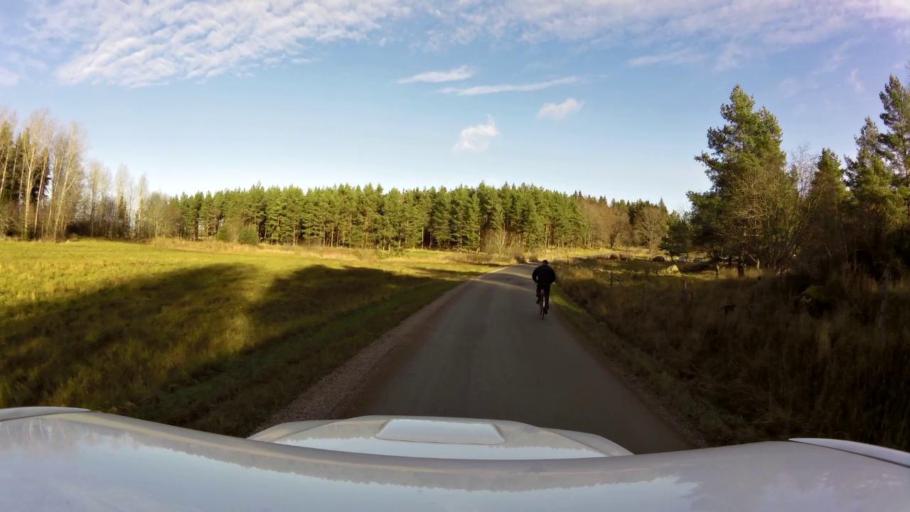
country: SE
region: OEstergoetland
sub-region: Linkopings Kommun
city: Linkoping
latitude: 58.3617
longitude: 15.6015
